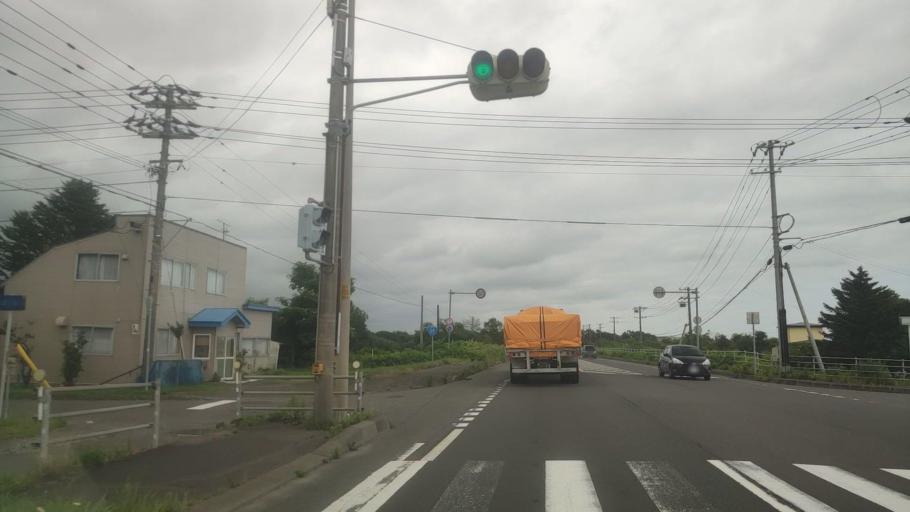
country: JP
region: Hokkaido
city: Shiraoi
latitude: 42.5202
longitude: 141.3071
